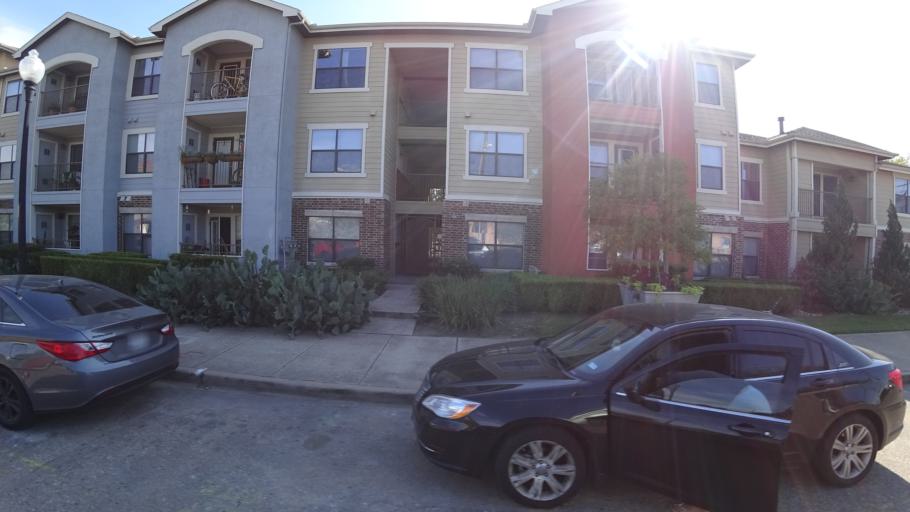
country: US
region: Texas
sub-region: Travis County
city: Austin
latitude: 30.2611
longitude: -97.7210
